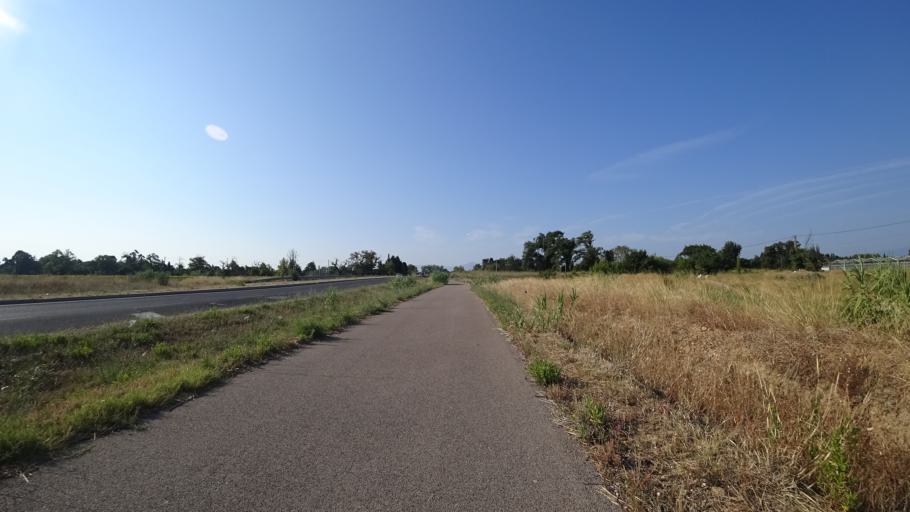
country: FR
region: Languedoc-Roussillon
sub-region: Departement des Pyrenees-Orientales
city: Perpignan
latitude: 42.7225
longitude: 2.9026
